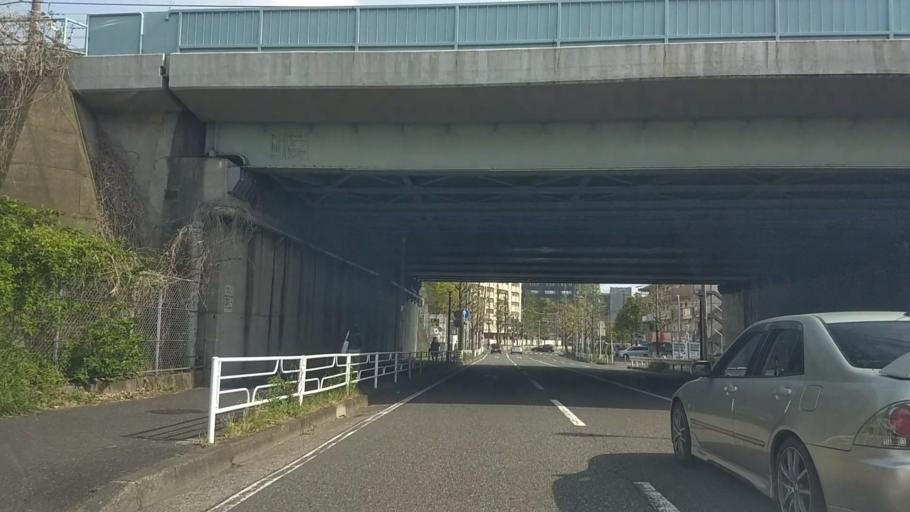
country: JP
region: Kanagawa
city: Kamakura
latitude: 35.3680
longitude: 139.5480
